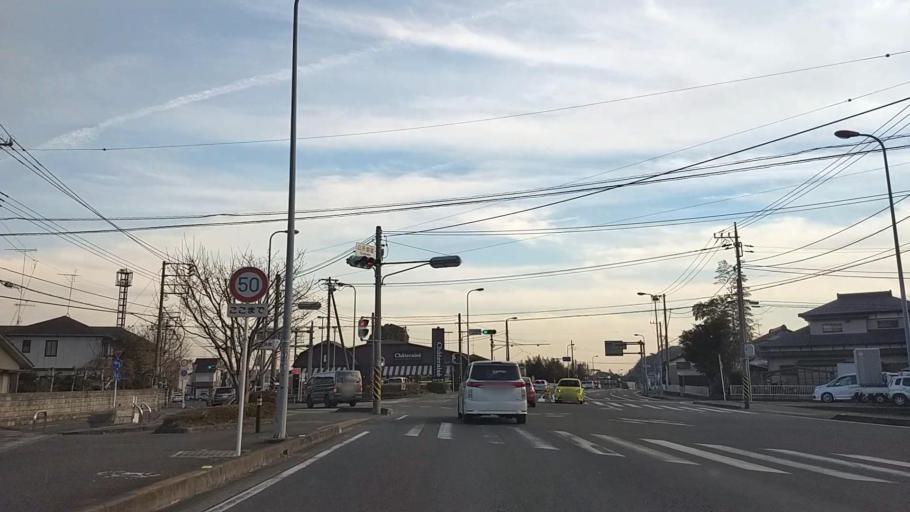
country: JP
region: Kanagawa
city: Atsugi
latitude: 35.4850
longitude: 139.3290
